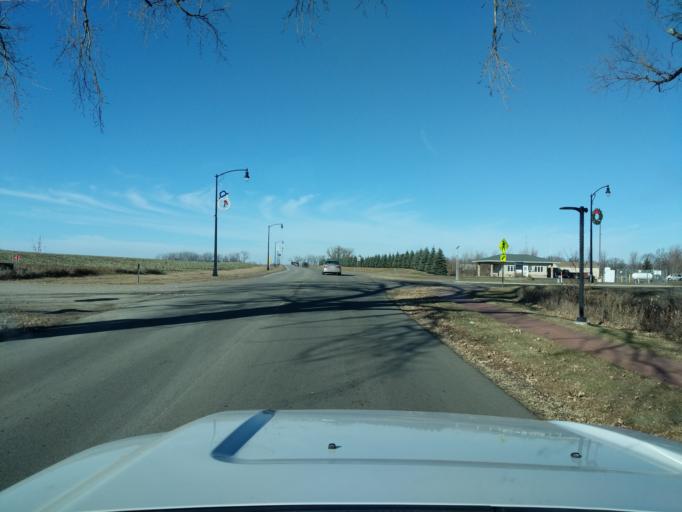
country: US
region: Minnesota
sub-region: Yellow Medicine County
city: Granite Falls
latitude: 44.7635
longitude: -95.5286
